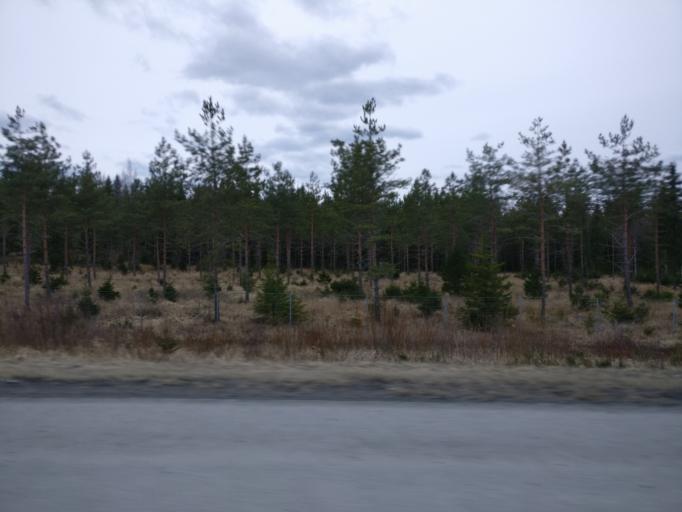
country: FI
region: Haeme
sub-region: Haemeenlinna
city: Kalvola
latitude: 61.1325
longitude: 24.0980
